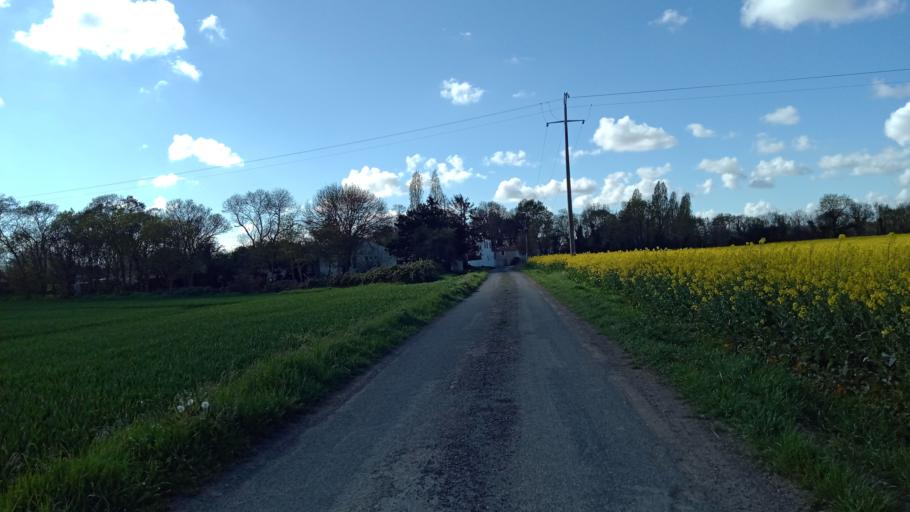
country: FR
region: Poitou-Charentes
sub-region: Departement de la Charente-Maritime
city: Verines
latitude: 46.1670
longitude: -0.9418
